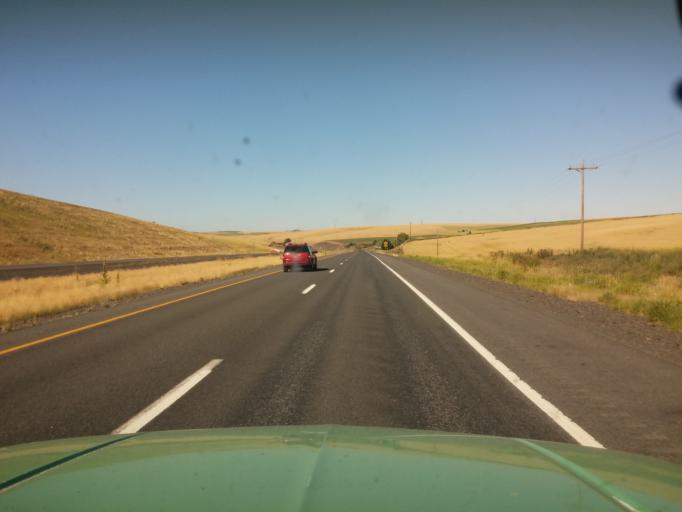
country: US
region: Idaho
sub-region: Nez Perce County
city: Lewiston
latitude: 46.4915
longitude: -117.0185
